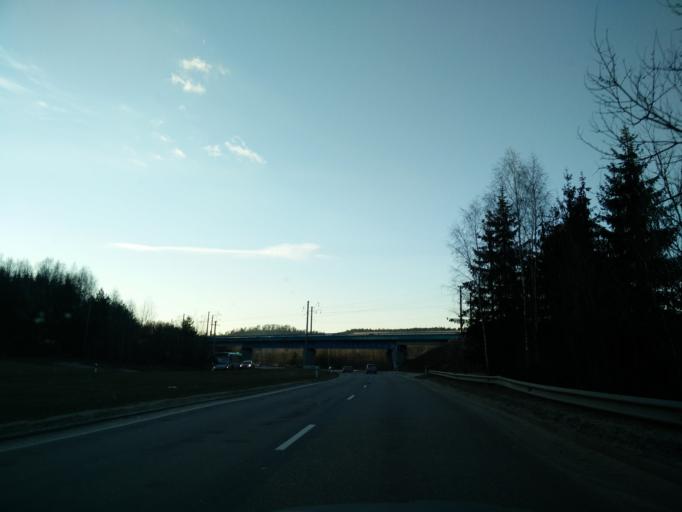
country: LT
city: Skaidiskes
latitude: 54.6919
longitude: 25.3913
